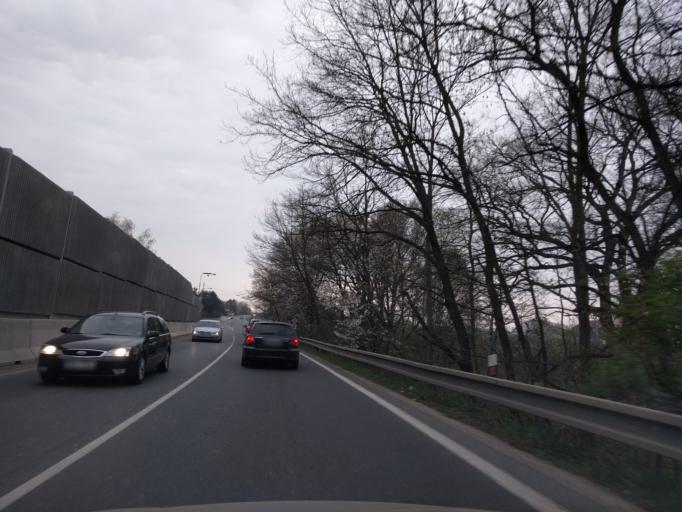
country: CZ
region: Central Bohemia
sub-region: Okres Praha-Vychod
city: Ricany
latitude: 49.9972
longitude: 14.6502
